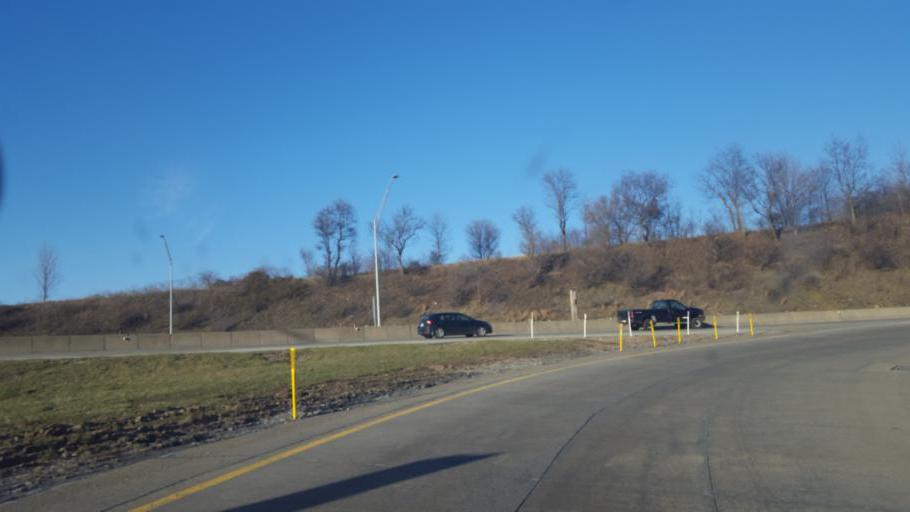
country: US
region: Pennsylvania
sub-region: Westmoreland County
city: New Stanton
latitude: 40.2239
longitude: -79.6049
